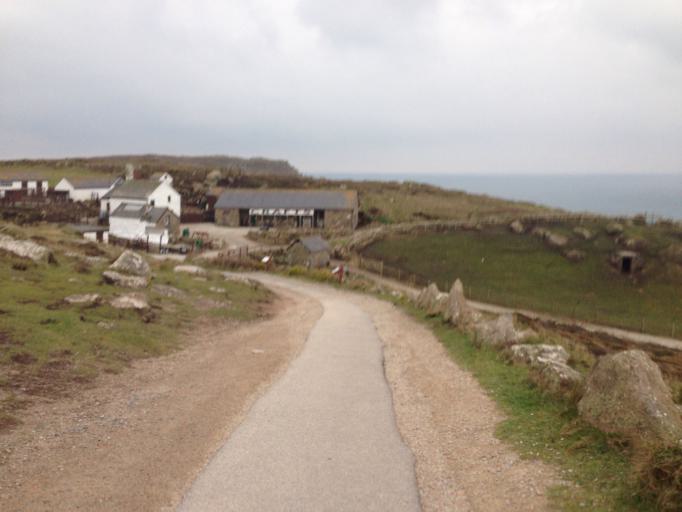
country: GB
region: England
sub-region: Cornwall
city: Sennen
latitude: 50.0632
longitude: -5.7113
